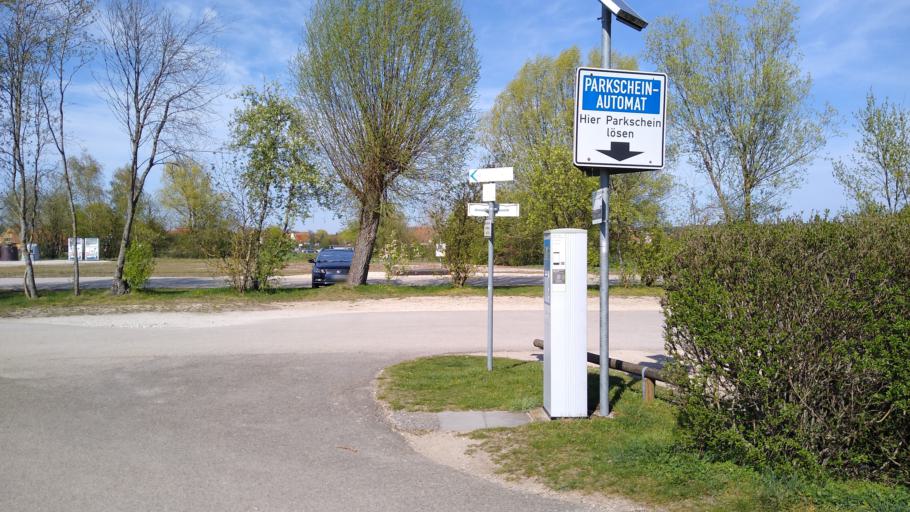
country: DE
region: Bavaria
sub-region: Regierungsbezirk Mittelfranken
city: Muhr am See
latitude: 49.1494
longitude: 10.7109
